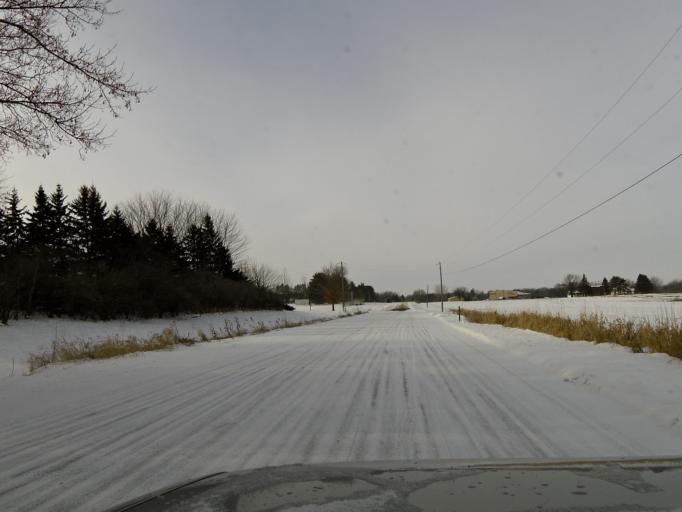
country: US
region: Minnesota
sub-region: Carver County
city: Mayer
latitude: 44.8912
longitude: -93.8796
